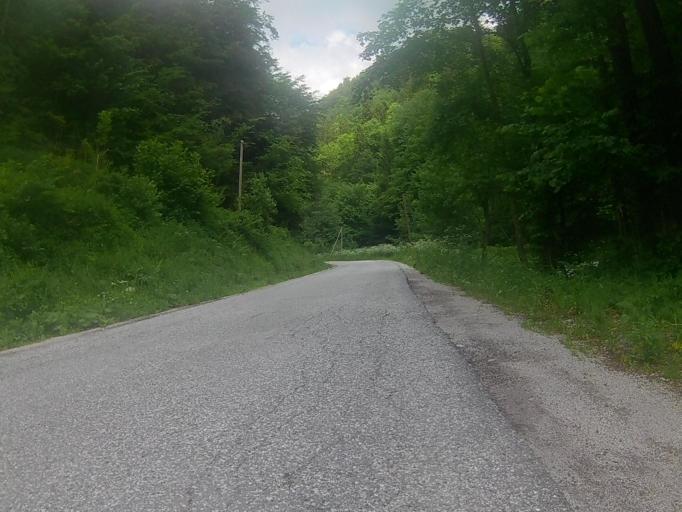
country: SI
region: Maribor
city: Bresternica
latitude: 46.5982
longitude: 15.5550
